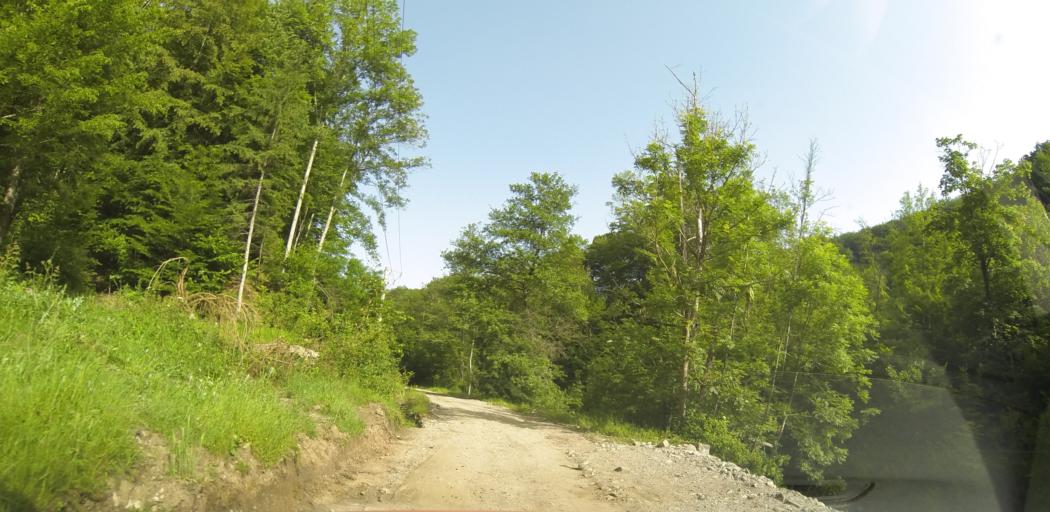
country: RO
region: Valcea
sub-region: Oras Baile Olanesti
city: Baile Olanesti
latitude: 45.2203
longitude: 24.2151
